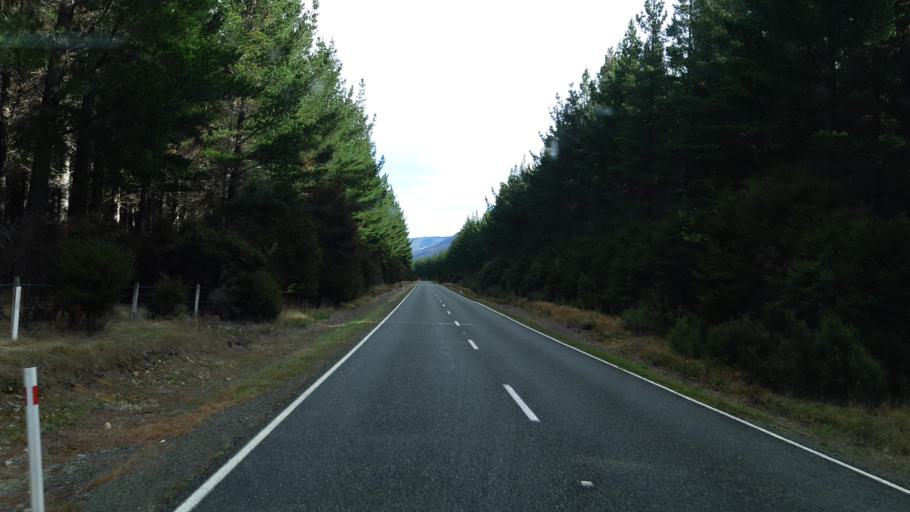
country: NZ
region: Tasman
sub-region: Tasman District
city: Wakefield
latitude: -41.7179
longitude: 173.0734
